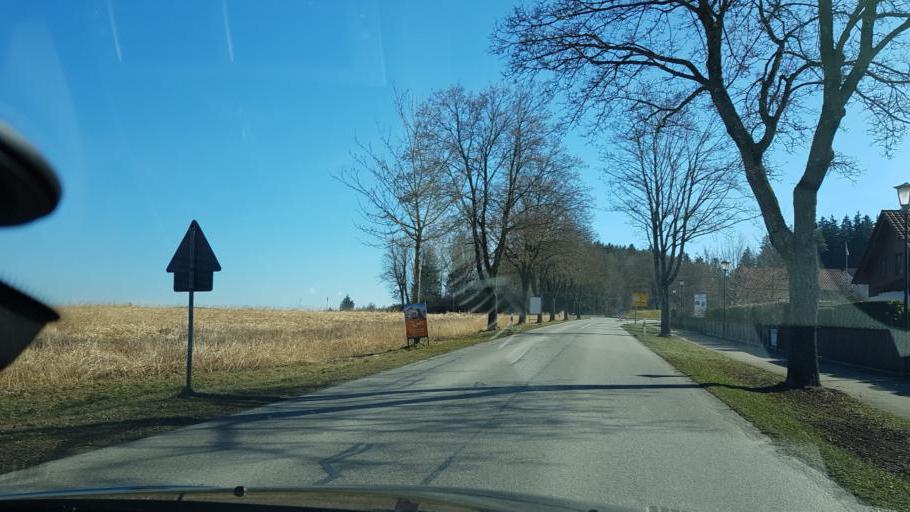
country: DE
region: Bavaria
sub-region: Upper Bavaria
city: Oberschweinbach
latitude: 48.2347
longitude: 11.1623
